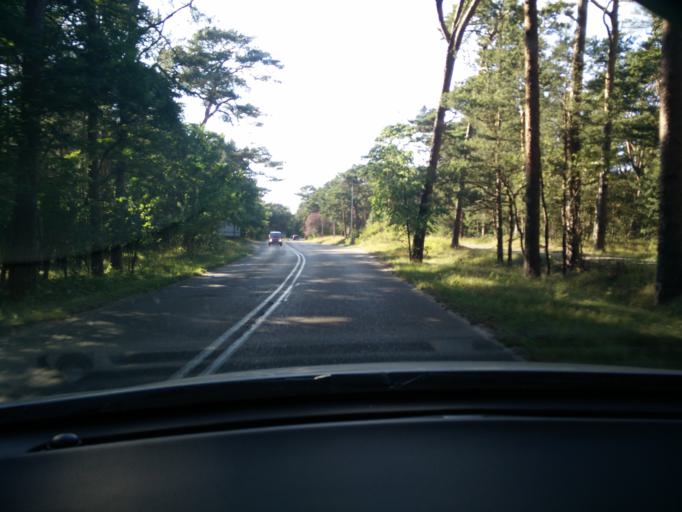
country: PL
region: Pomeranian Voivodeship
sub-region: Powiat pucki
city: Jastarnia
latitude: 54.6724
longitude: 18.7315
